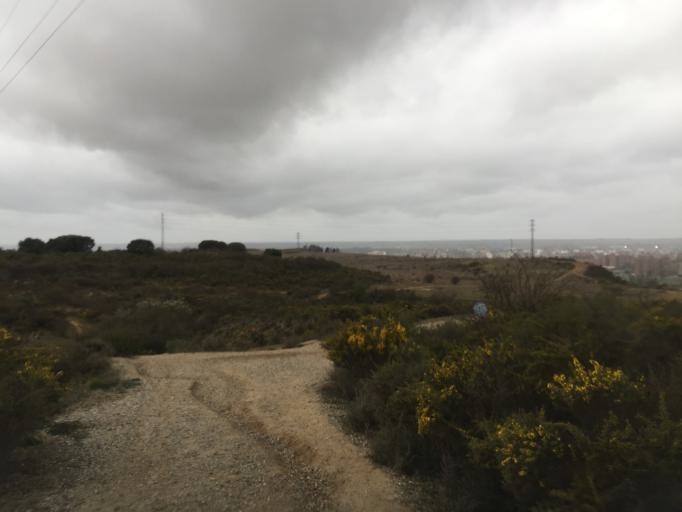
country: ES
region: Castille and Leon
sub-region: Provincia de Leon
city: Leon
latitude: 42.5950
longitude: -5.5421
